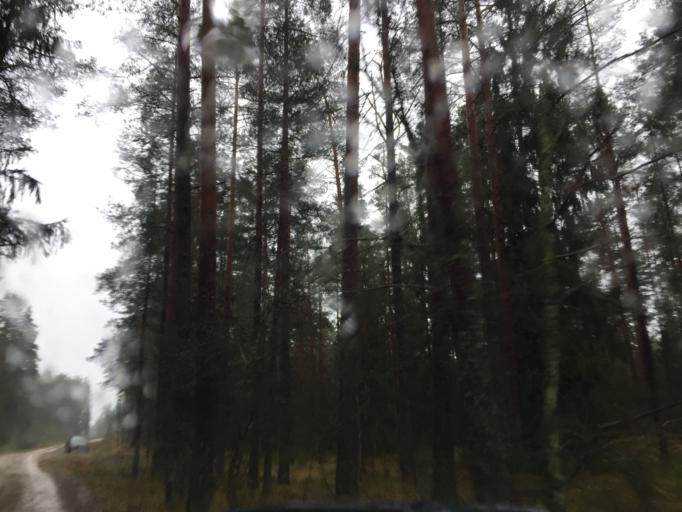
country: LV
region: Salas
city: Sala
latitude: 56.5111
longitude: 25.6964
